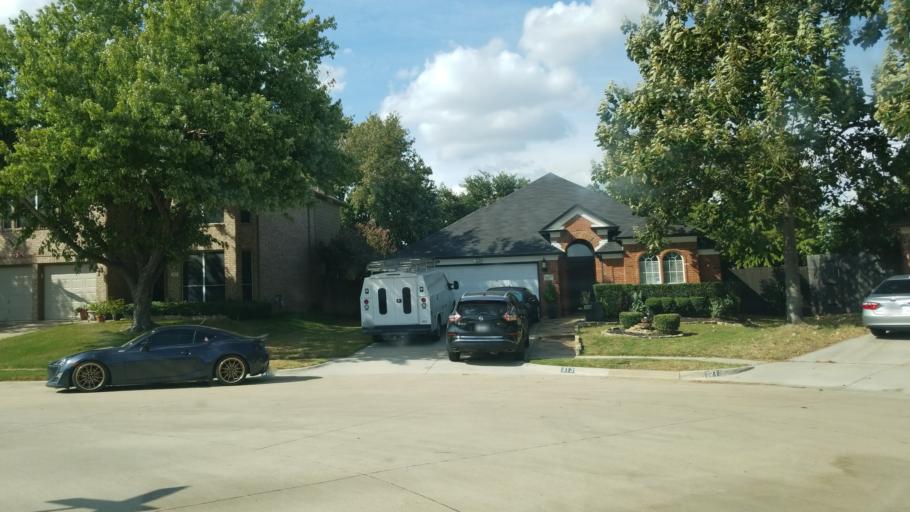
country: US
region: Texas
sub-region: Tarrant County
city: Euless
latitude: 32.8549
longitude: -97.0776
